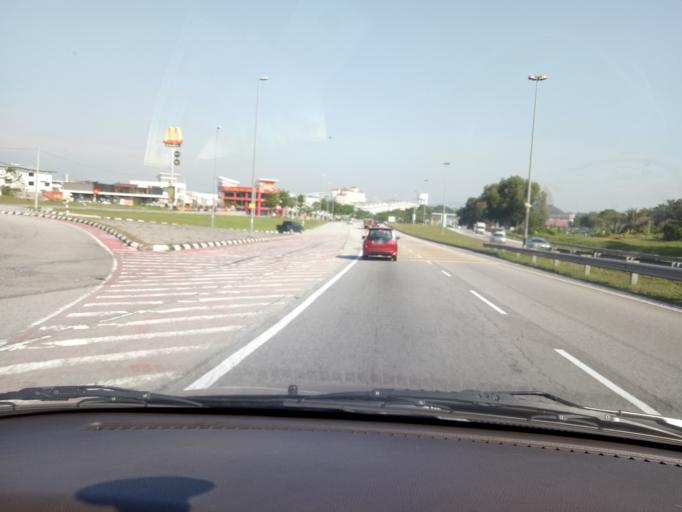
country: MY
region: Selangor
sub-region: Hulu Langat
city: Semenyih
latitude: 2.9886
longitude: 101.8220
